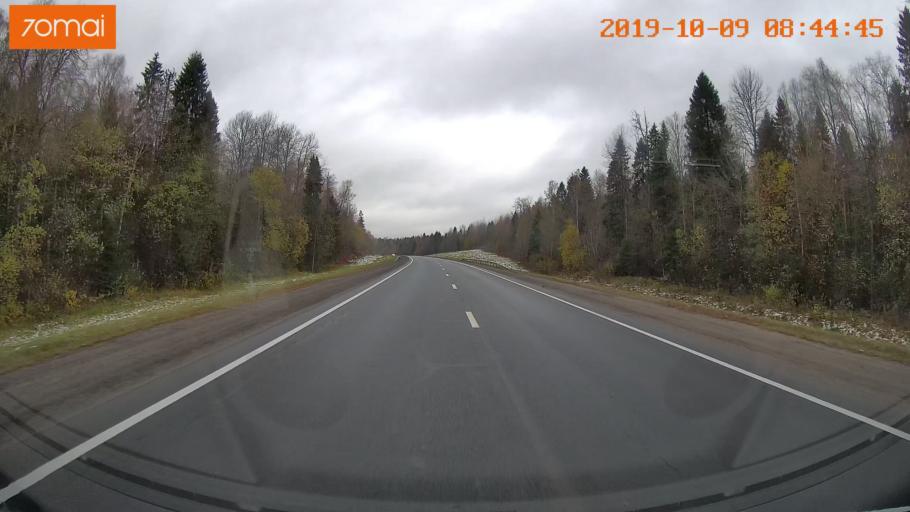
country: RU
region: Vologda
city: Gryazovets
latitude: 59.0404
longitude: 40.1044
